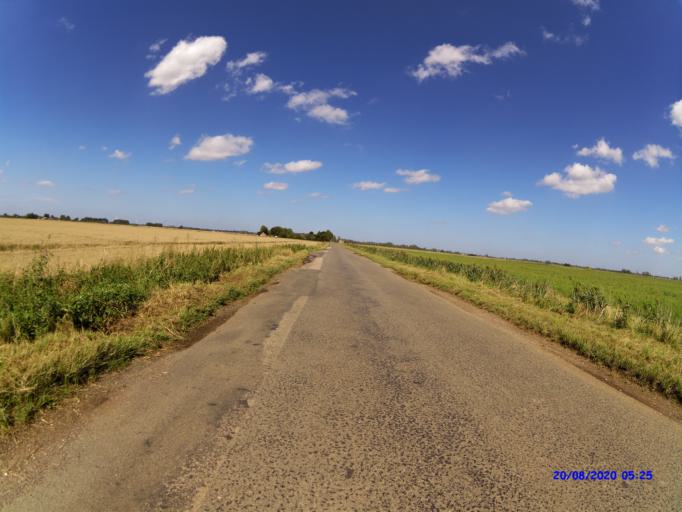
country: GB
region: England
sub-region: Cambridgeshire
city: Whittlesey
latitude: 52.5299
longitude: -0.1026
